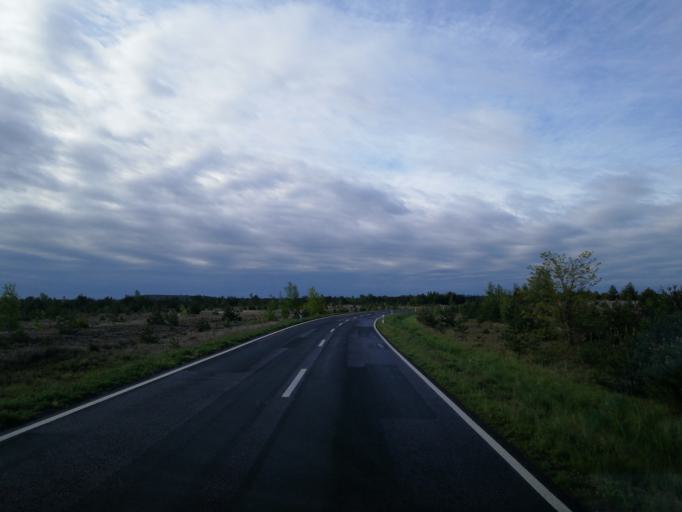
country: DE
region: Brandenburg
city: Sallgast
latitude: 51.5683
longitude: 13.7787
